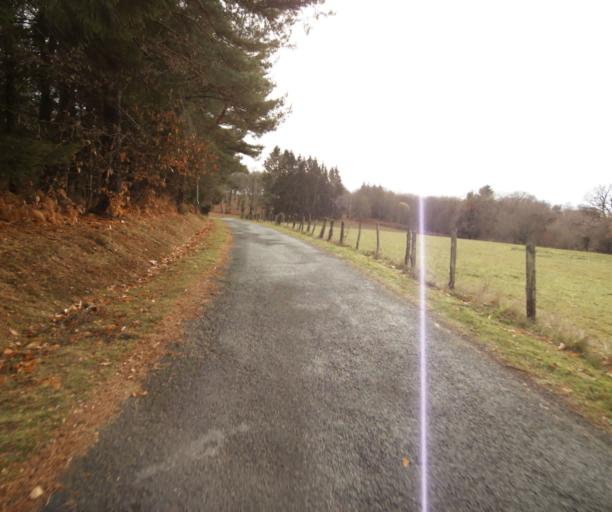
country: FR
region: Limousin
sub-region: Departement de la Correze
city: Saint-Mexant
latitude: 45.2772
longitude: 1.6786
